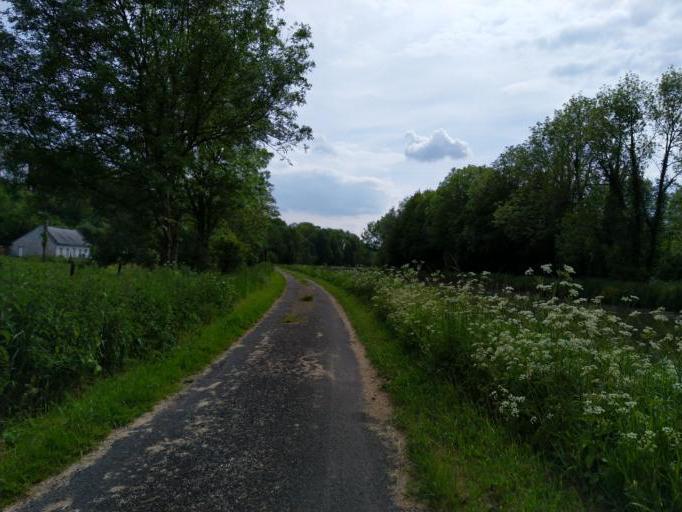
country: FR
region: Picardie
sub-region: Departement de l'Aisne
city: Etreux
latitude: 49.9694
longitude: 3.6246
